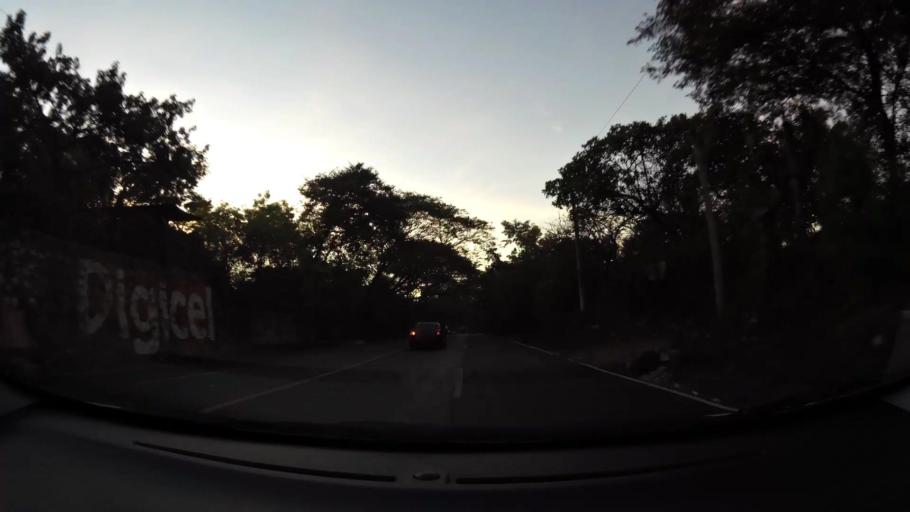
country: SV
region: San Miguel
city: San Miguel
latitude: 13.5014
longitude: -88.2169
